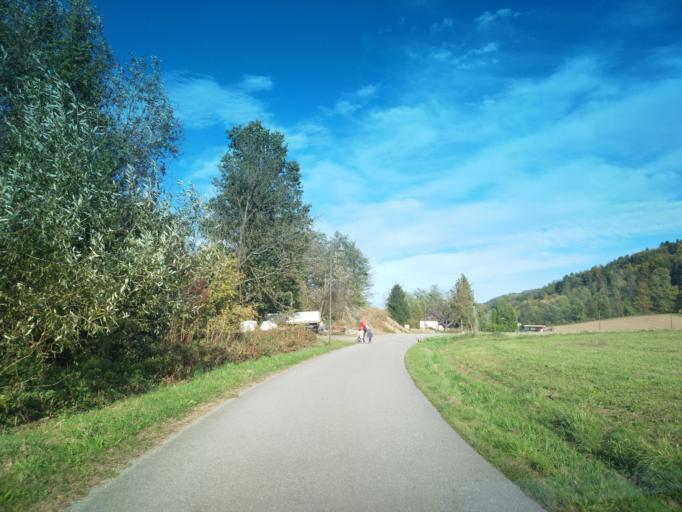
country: AT
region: Styria
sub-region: Politischer Bezirk Deutschlandsberg
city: Wies
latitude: 46.7233
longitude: 15.2999
